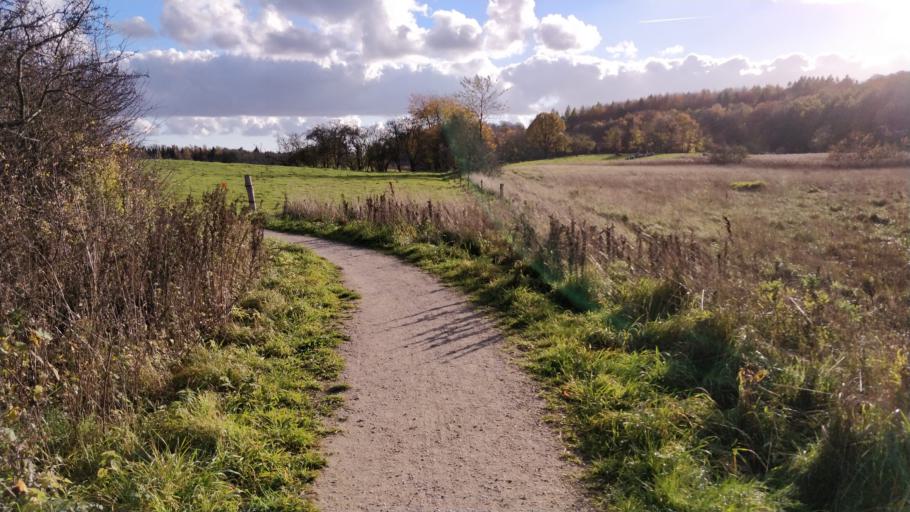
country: DK
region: Capital Region
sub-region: Rudersdal Kommune
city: Birkerod
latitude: 55.8368
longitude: 12.4429
